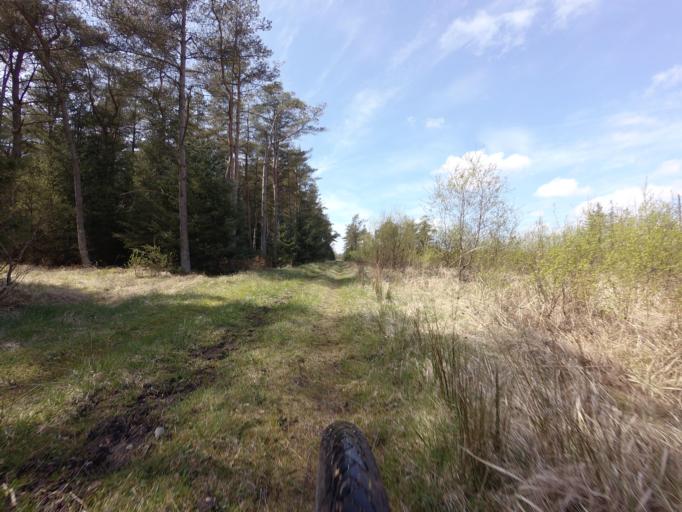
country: DK
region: North Denmark
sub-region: Jammerbugt Kommune
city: Brovst
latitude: 57.1651
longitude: 9.5497
